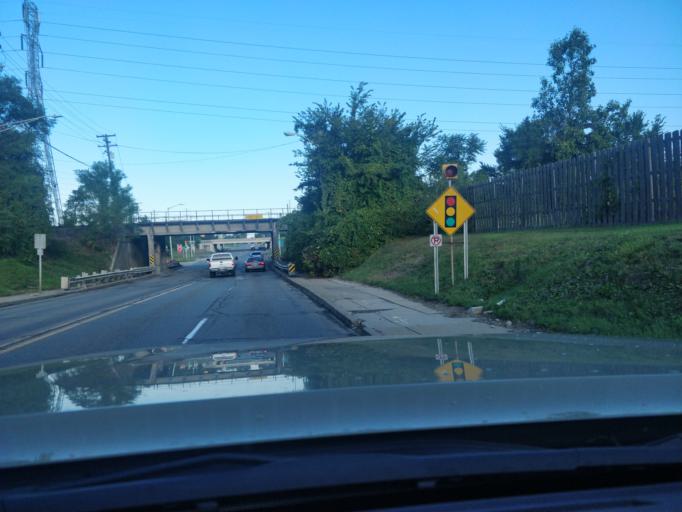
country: US
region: Michigan
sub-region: Wayne County
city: Melvindale
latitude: 42.2837
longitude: -83.1929
